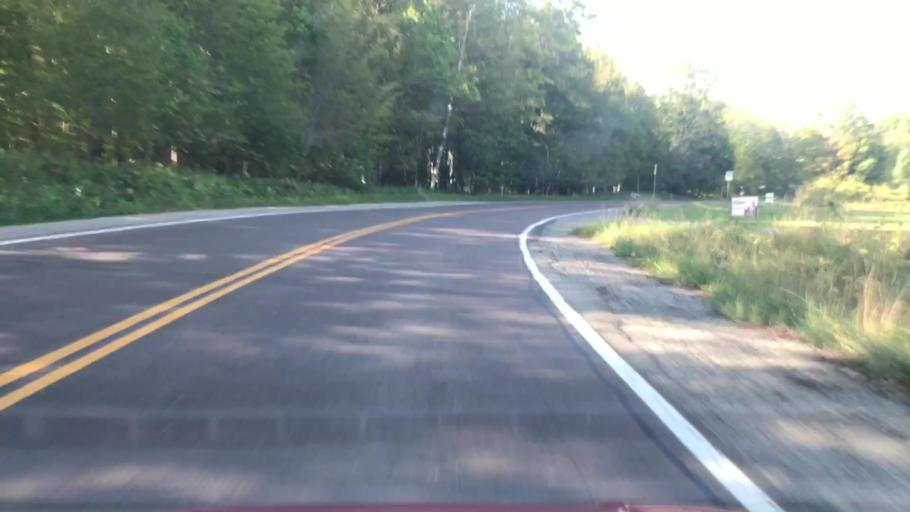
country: US
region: Michigan
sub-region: Chippewa County
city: Sault Ste. Marie
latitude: 46.2808
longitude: -84.0321
